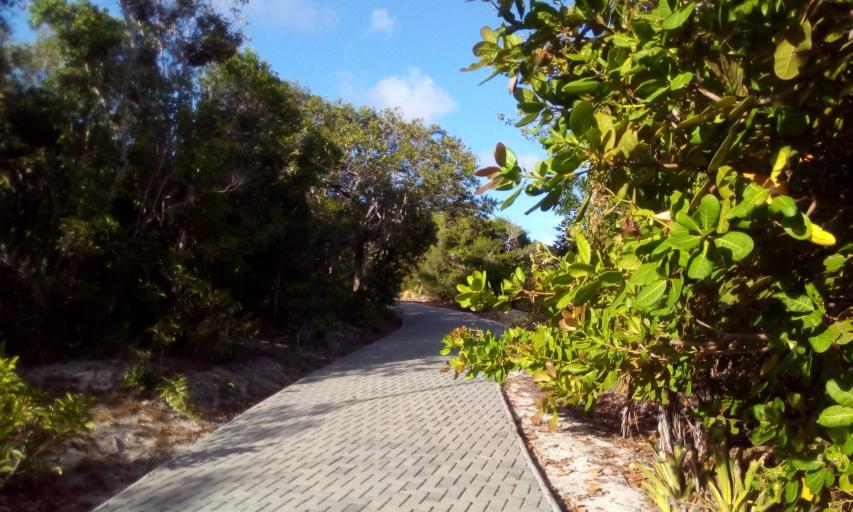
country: BR
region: Bahia
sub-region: Mata De Sao Joao
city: Mata de Sao Joao
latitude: -12.5718
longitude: -38.0073
